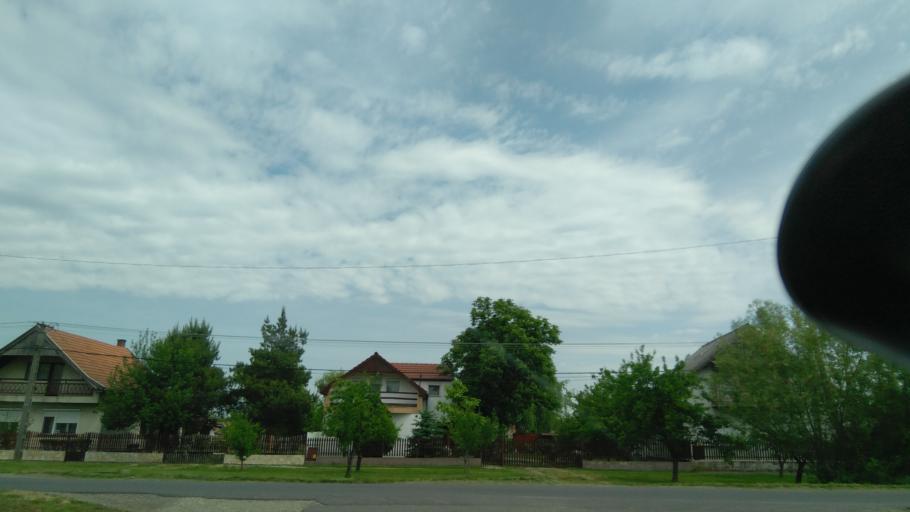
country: HU
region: Bekes
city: Fuzesgyarmat
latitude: 47.1026
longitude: 21.2169
